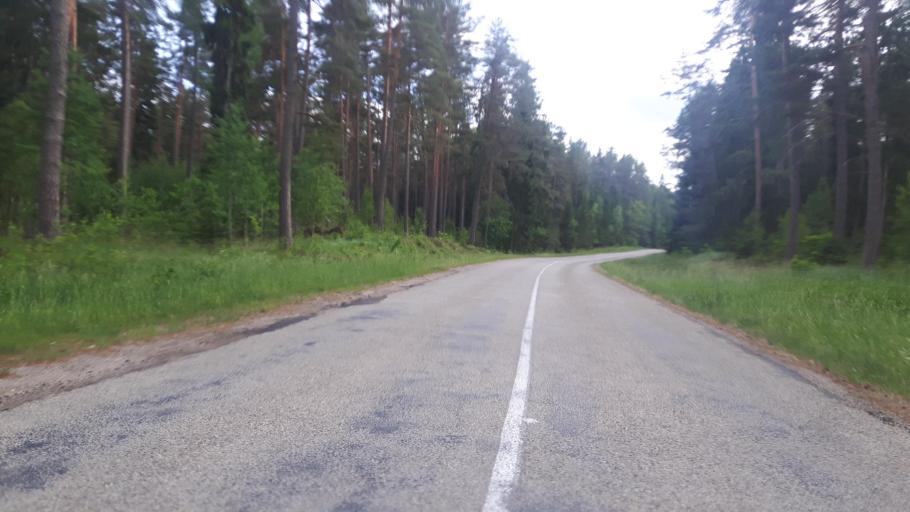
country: LV
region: Engure
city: Smarde
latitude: 57.0026
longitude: 23.3314
